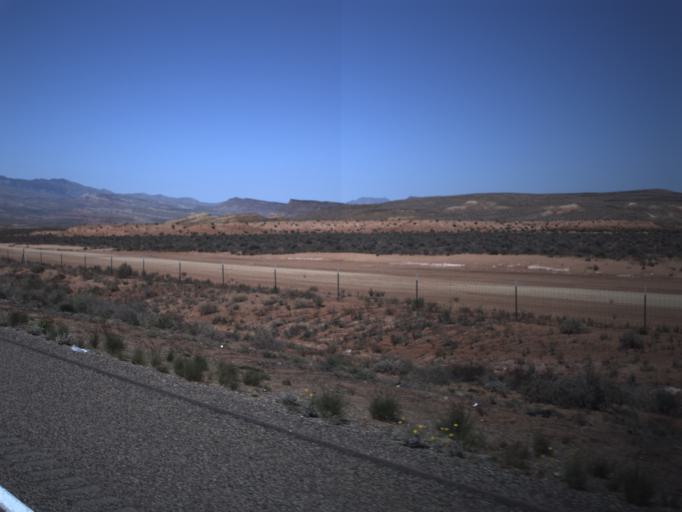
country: US
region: Utah
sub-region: Washington County
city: Saint George
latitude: 37.0015
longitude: -113.5757
